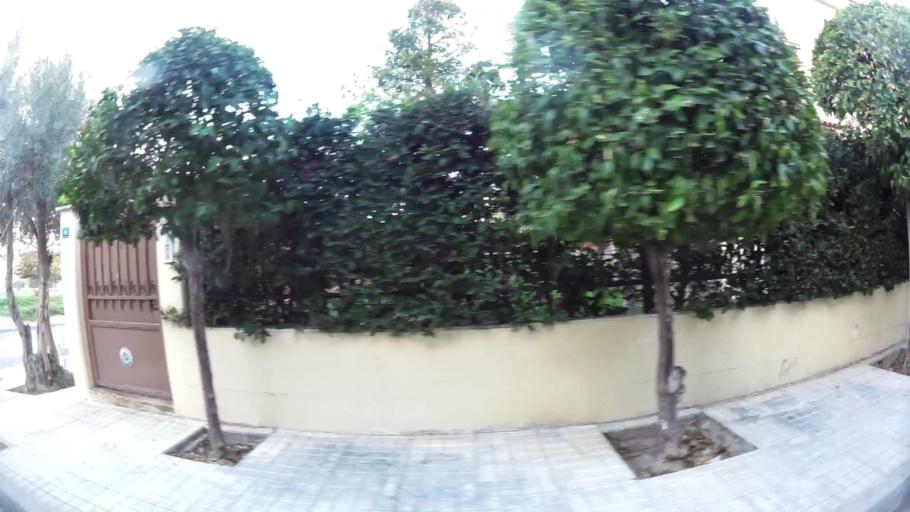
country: GR
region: Attica
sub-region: Nomarchia Athinas
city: Vrilissia
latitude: 38.0406
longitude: 23.8151
